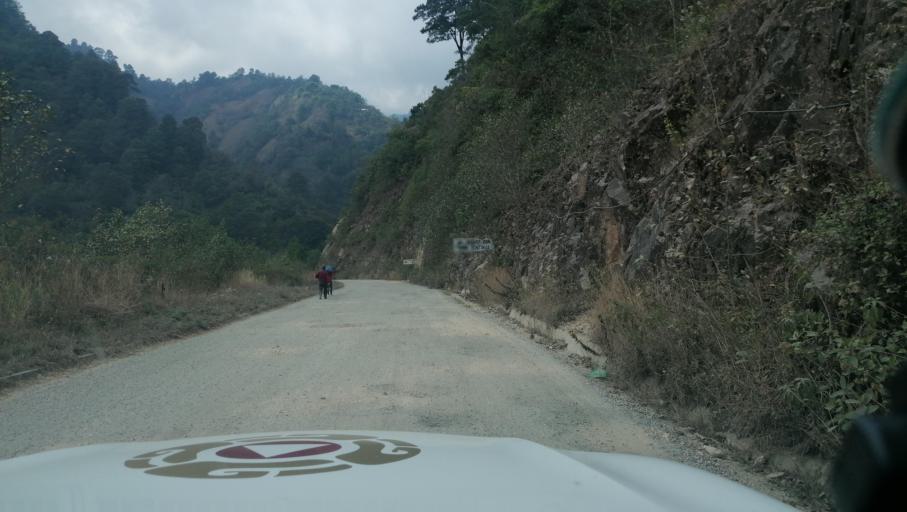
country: GT
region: San Marcos
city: Tacana
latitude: 15.2140
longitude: -92.2008
